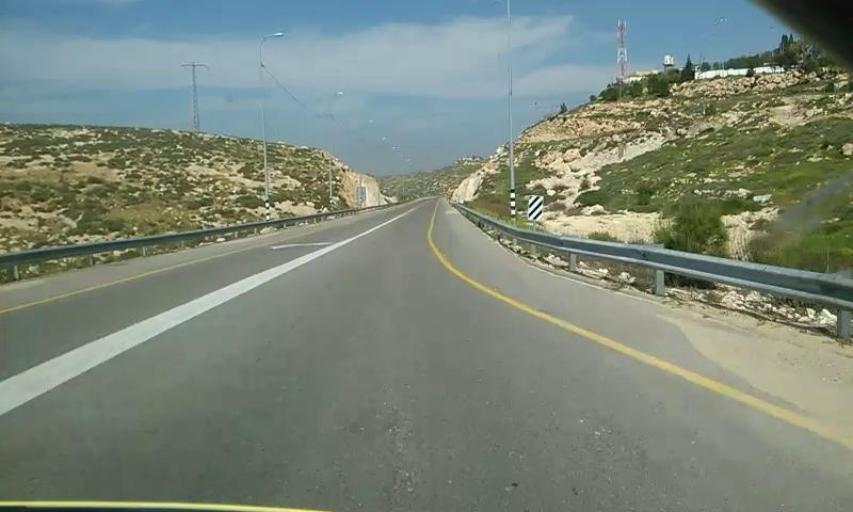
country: PS
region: West Bank
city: Az Zahiriyah
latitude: 31.3874
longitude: 35.0088
